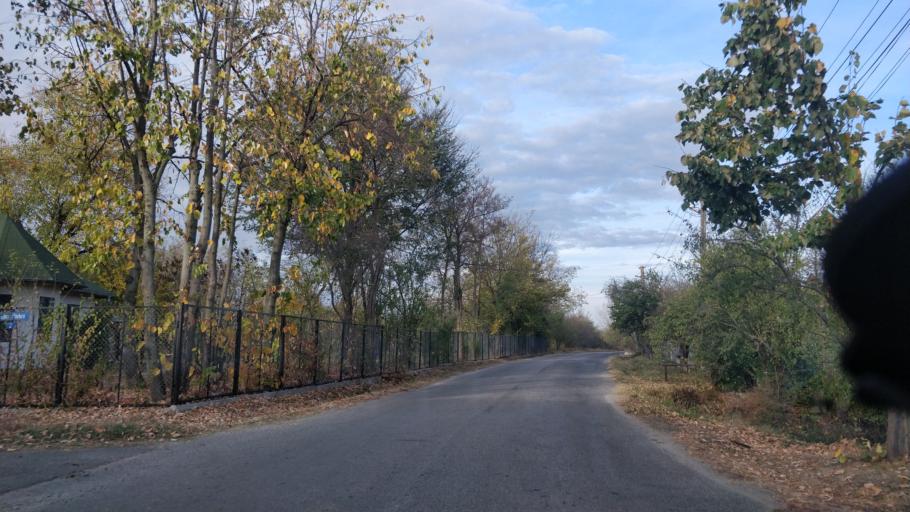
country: RO
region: Giurgiu
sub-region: Comuna Bucsani
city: Bucsani
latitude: 44.3525
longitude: 25.6560
